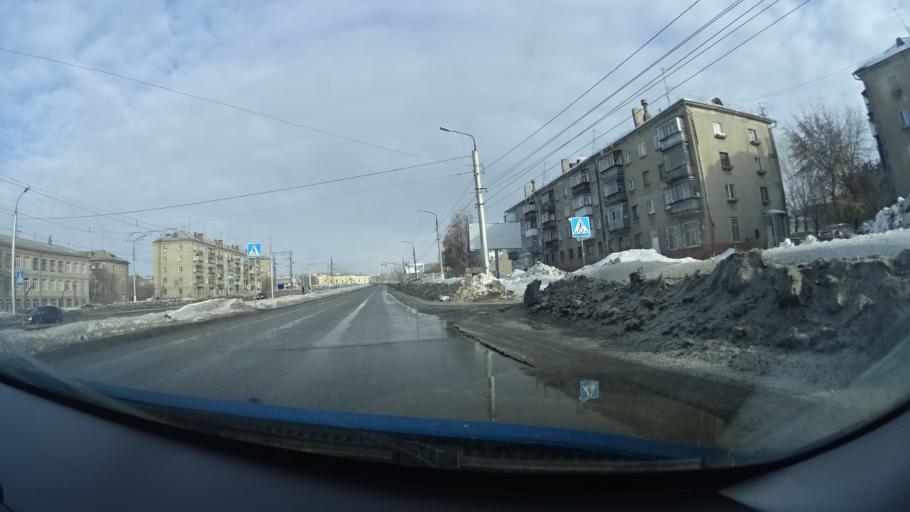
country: RU
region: Chelyabinsk
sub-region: Gorod Magnitogorsk
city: Magnitogorsk
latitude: 53.4344
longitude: 58.9854
